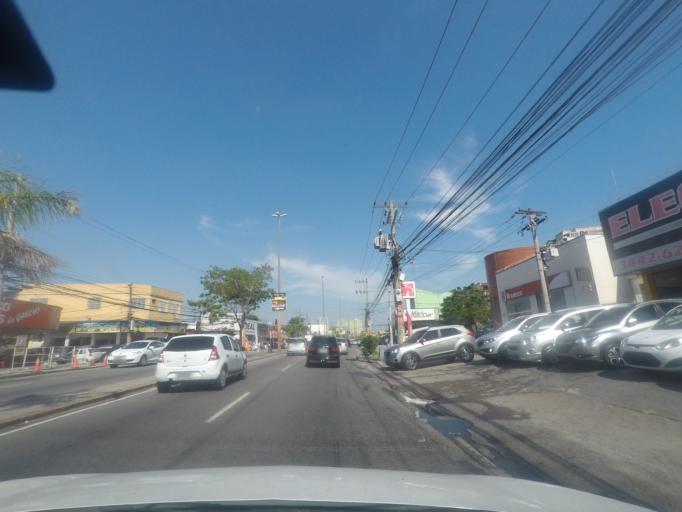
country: BR
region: Rio de Janeiro
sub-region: Sao Joao De Meriti
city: Sao Joao de Meriti
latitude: -22.8780
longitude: -43.3608
